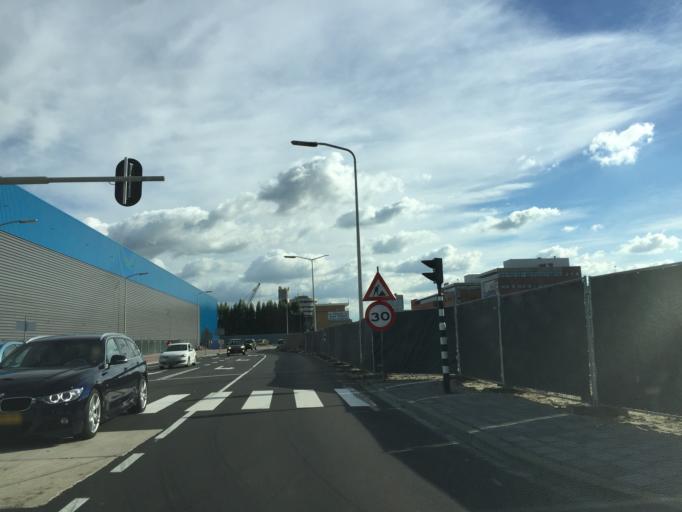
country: NL
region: South Holland
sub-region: Gemeente Leidschendam-Voorburg
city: Voorburg
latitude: 52.0668
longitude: 4.3406
